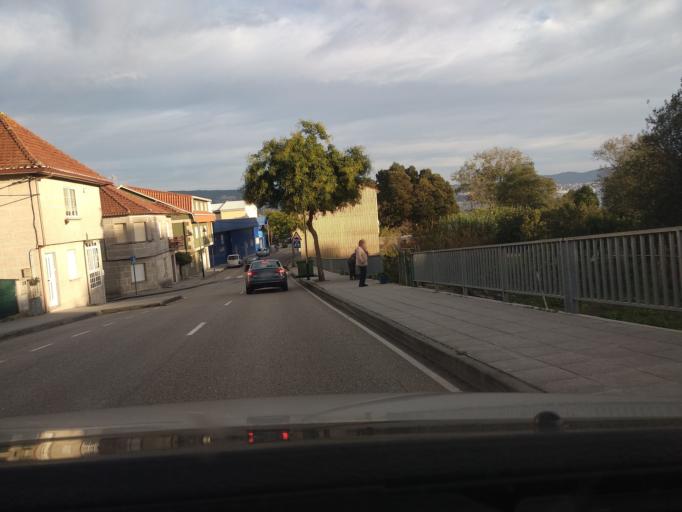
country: ES
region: Galicia
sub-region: Provincia de Pontevedra
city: Moana
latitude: 42.2892
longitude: -8.7323
